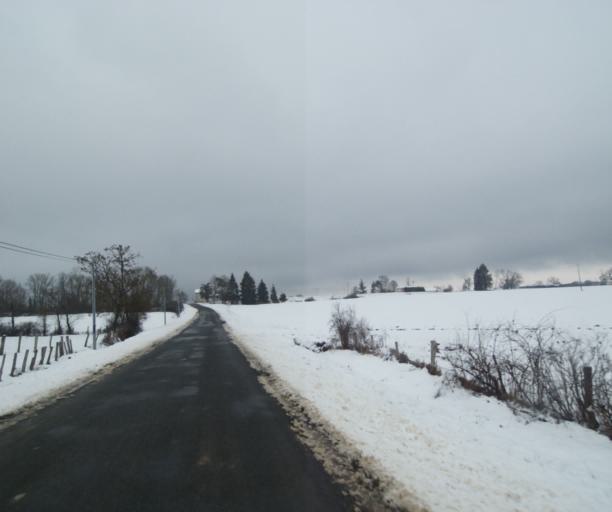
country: FR
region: Champagne-Ardenne
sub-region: Departement de la Haute-Marne
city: Laneuville-a-Remy
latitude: 48.4955
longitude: 4.8678
